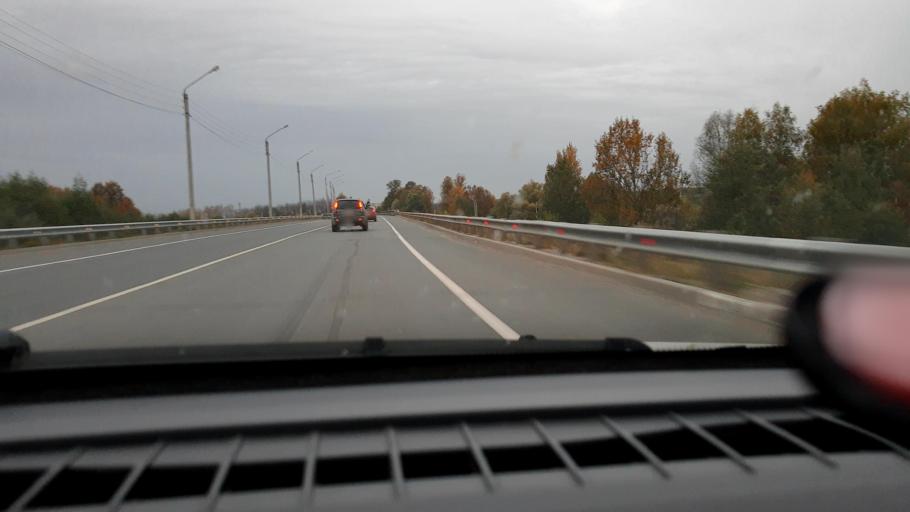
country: RU
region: Vladimir
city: Orgtrud
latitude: 56.2104
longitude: 40.5903
